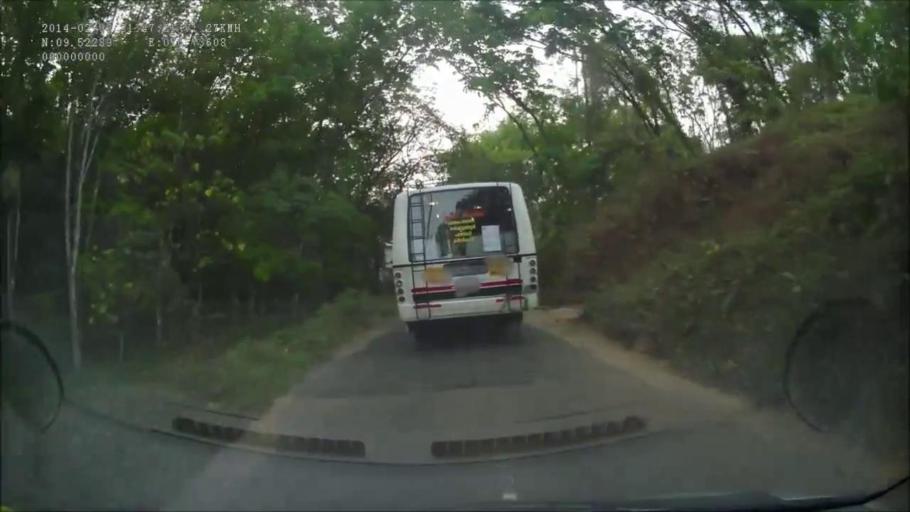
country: IN
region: Kerala
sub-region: Kottayam
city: Erattupetta
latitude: 9.5238
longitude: 76.7351
